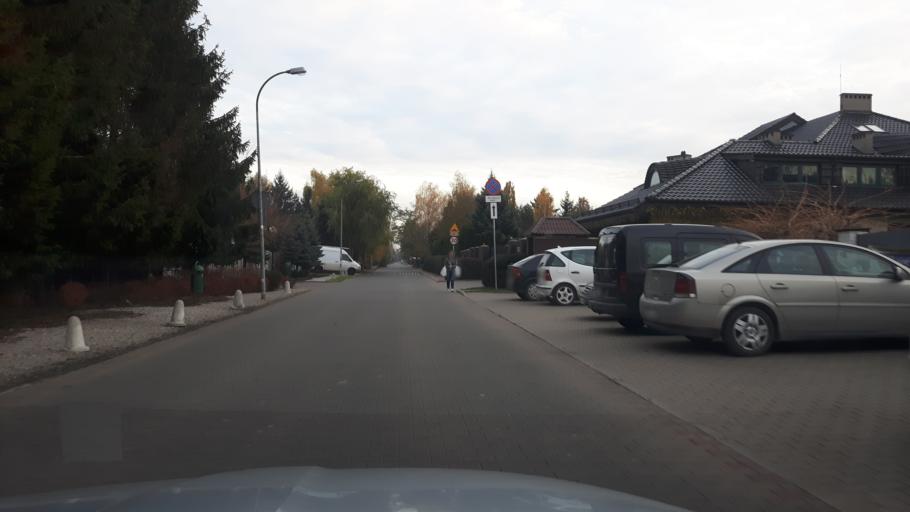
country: PL
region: Masovian Voivodeship
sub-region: Warszawa
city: Wilanow
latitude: 52.1706
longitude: 21.1144
